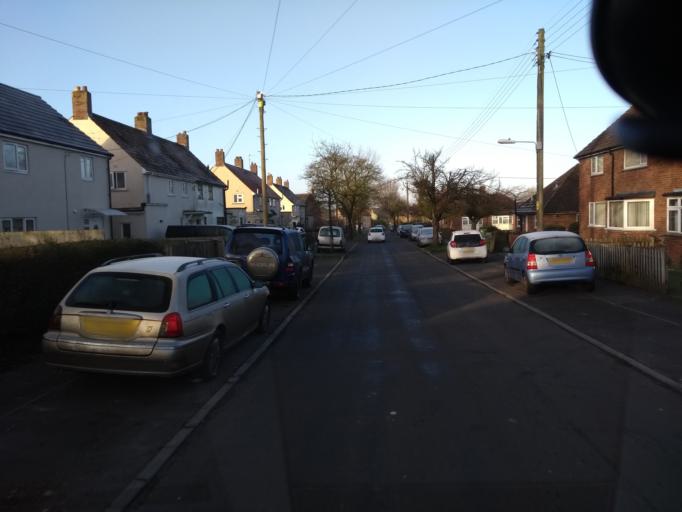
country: GB
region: England
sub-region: Somerset
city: Shepton Mallet
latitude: 51.1862
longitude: -2.5500
